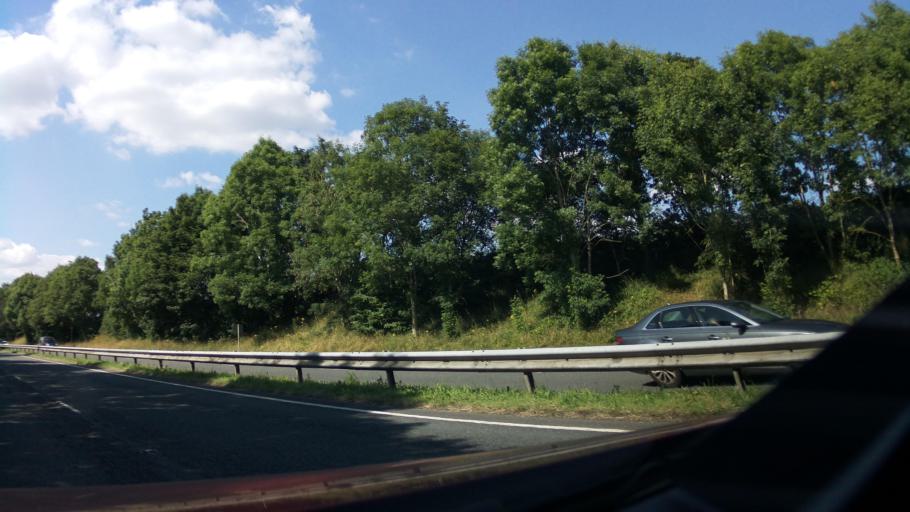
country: GB
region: England
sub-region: Worcestershire
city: Barnt Green
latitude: 52.3196
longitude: -2.0019
